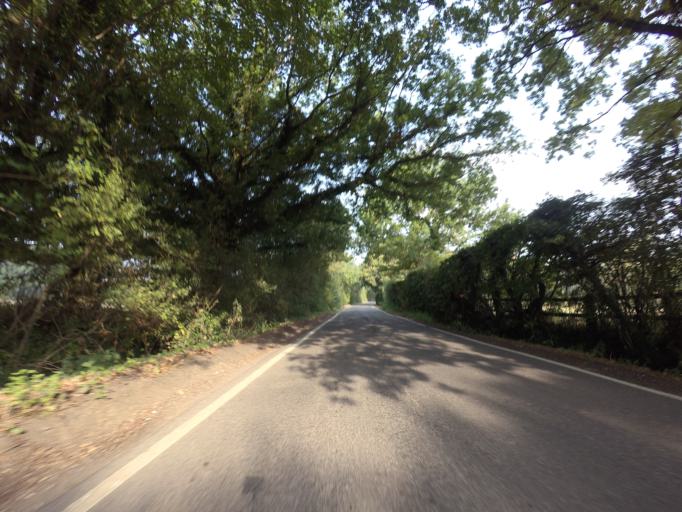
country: GB
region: England
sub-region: Kent
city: Tenterden
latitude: 51.1145
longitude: 0.6824
